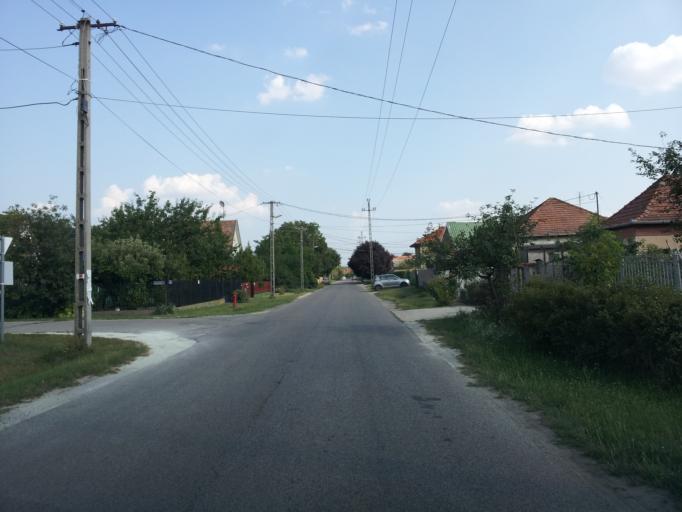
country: HU
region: Pest
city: Szigethalom
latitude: 47.3113
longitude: 19.0119
